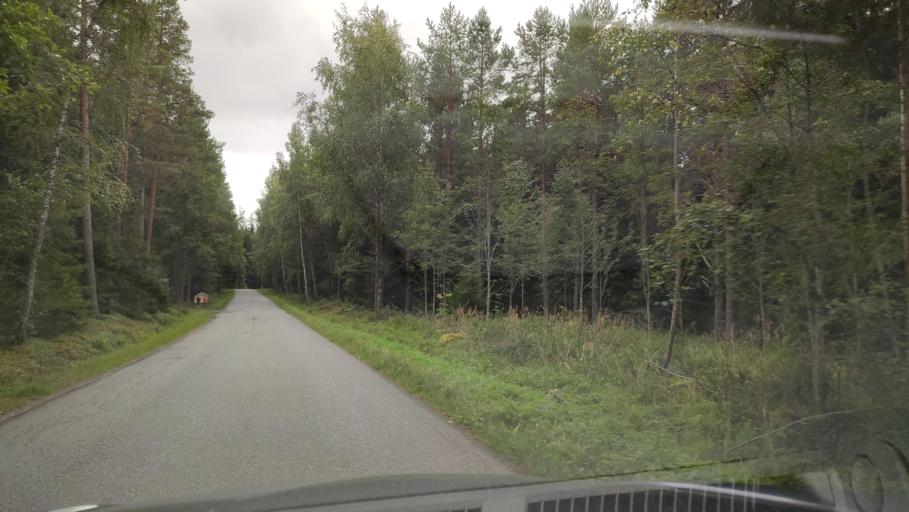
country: FI
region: Ostrobothnia
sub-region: Sydosterbotten
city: Kristinestad
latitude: 62.2509
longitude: 21.3510
